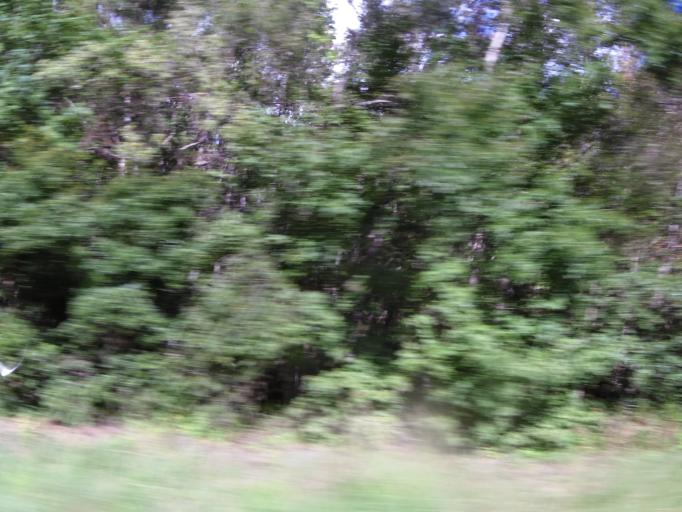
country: US
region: Georgia
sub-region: Camden County
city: Woodbine
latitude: 30.8983
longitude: -81.7095
